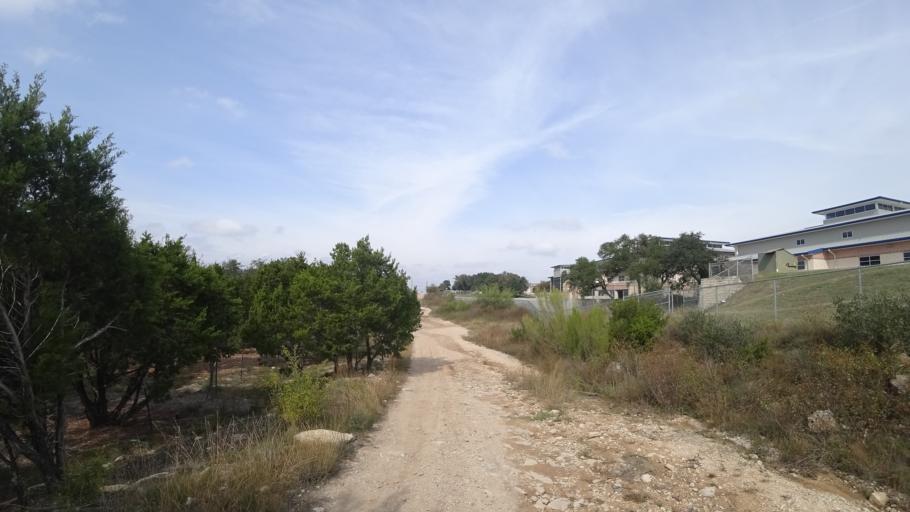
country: US
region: Texas
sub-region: Travis County
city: Hudson Bend
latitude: 30.3894
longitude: -97.9355
